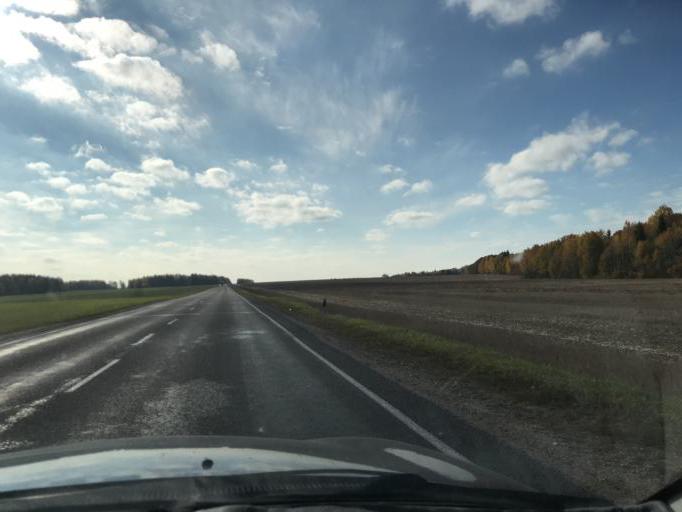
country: BY
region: Grodnenskaya
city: Voranava
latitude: 54.1996
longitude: 25.3473
